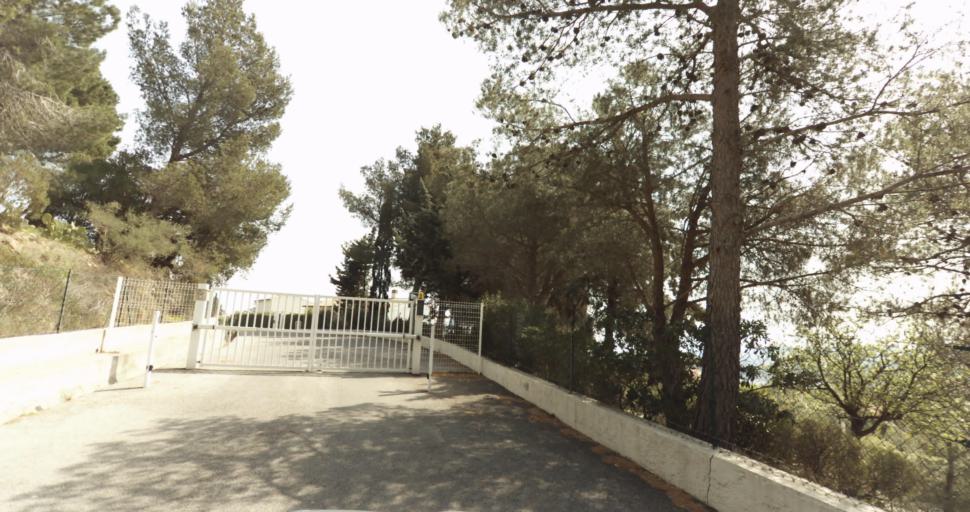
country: FR
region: Provence-Alpes-Cote d'Azur
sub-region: Departement du Var
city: Bormes-les-Mimosas
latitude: 43.1470
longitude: 6.3470
